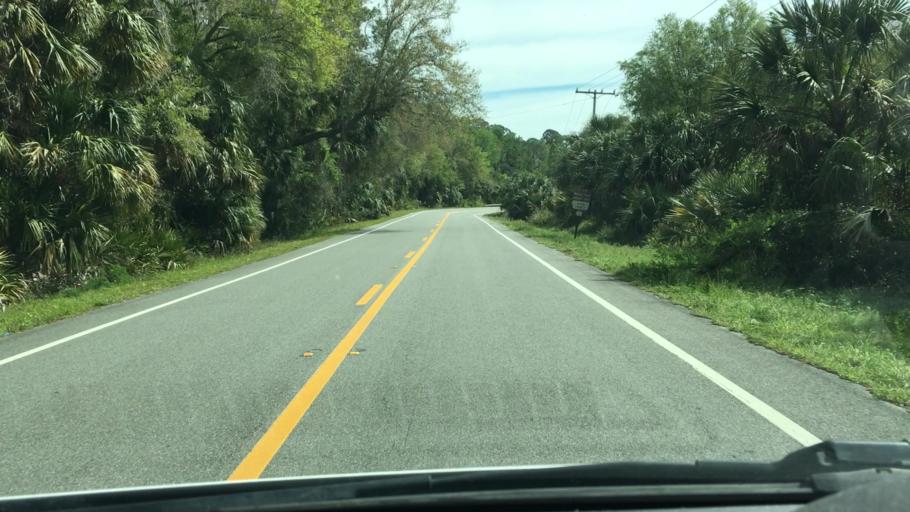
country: US
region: Florida
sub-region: Lake County
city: Lake Mack-Forest Hills
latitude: 29.0100
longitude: -81.3960
